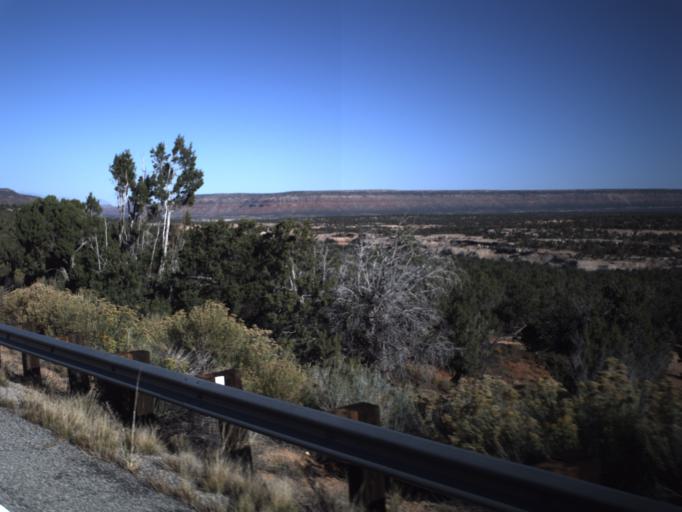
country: US
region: Utah
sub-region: San Juan County
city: Blanding
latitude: 37.5426
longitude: -109.9772
